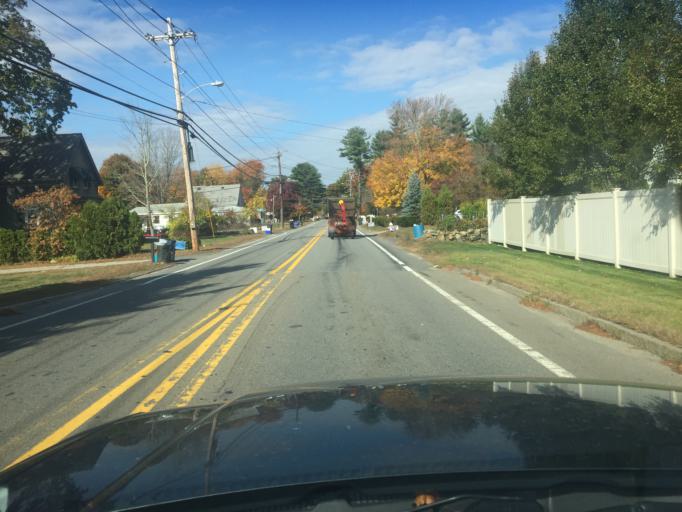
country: US
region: Massachusetts
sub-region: Norfolk County
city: Bellingham
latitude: 42.1043
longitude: -71.5045
